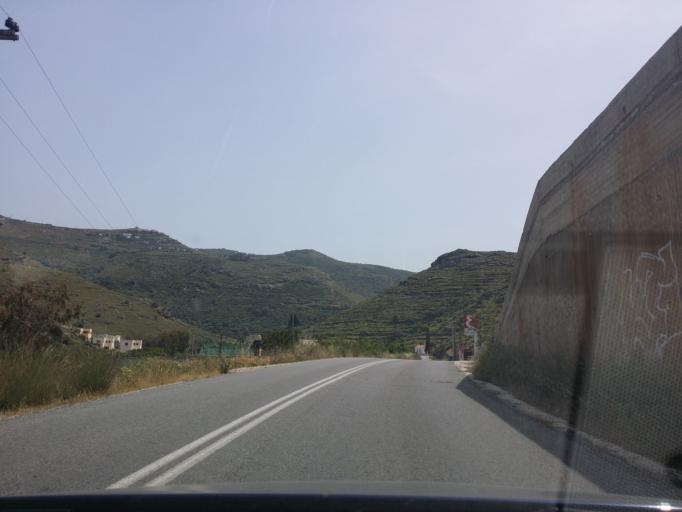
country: GR
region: South Aegean
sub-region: Nomos Kykladon
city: Kea
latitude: 37.6505
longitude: 24.3176
